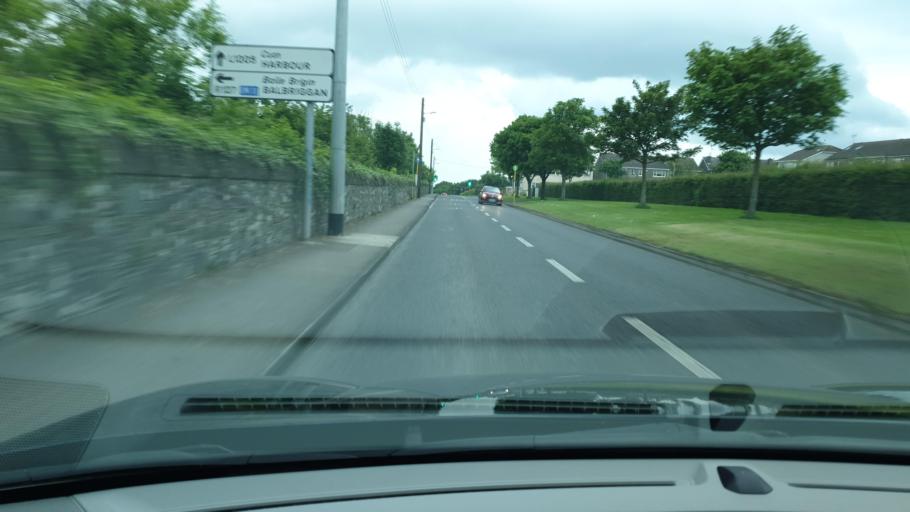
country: IE
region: Leinster
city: Balbriggan
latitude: 53.6046
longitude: -6.1701
